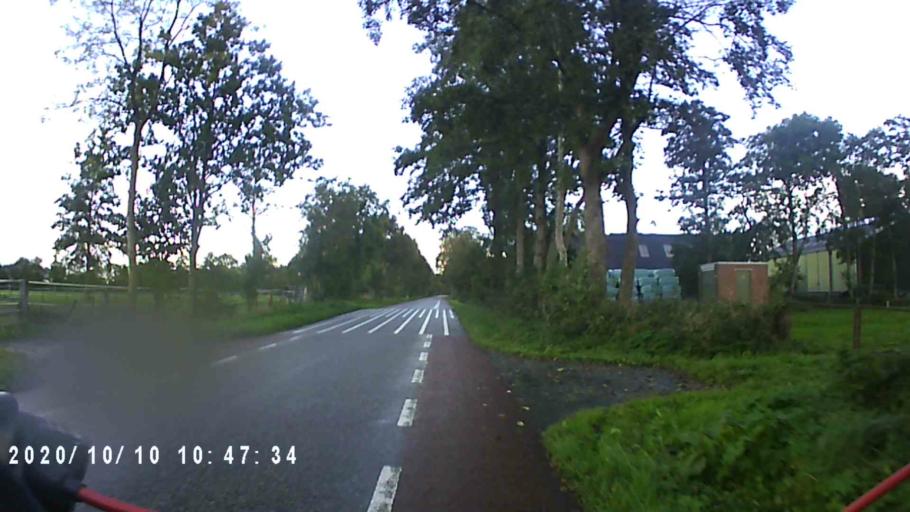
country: NL
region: Groningen
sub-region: Gemeente Grootegast
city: Grootegast
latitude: 53.1660
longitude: 6.2466
